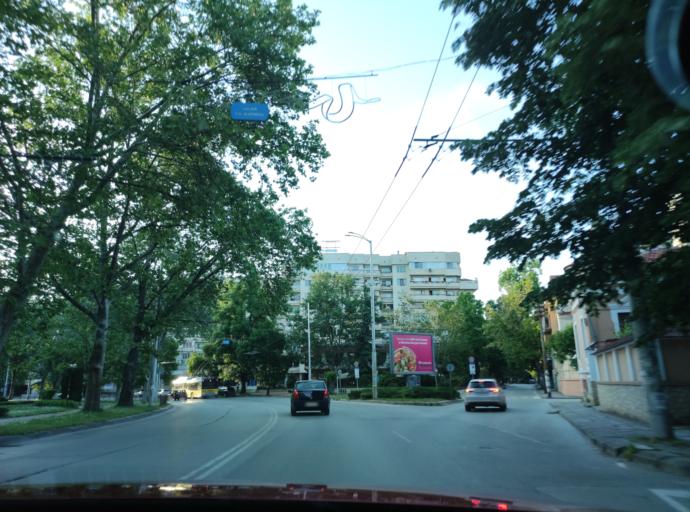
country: BG
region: Pleven
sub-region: Obshtina Pleven
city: Pleven
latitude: 43.4123
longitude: 24.6188
